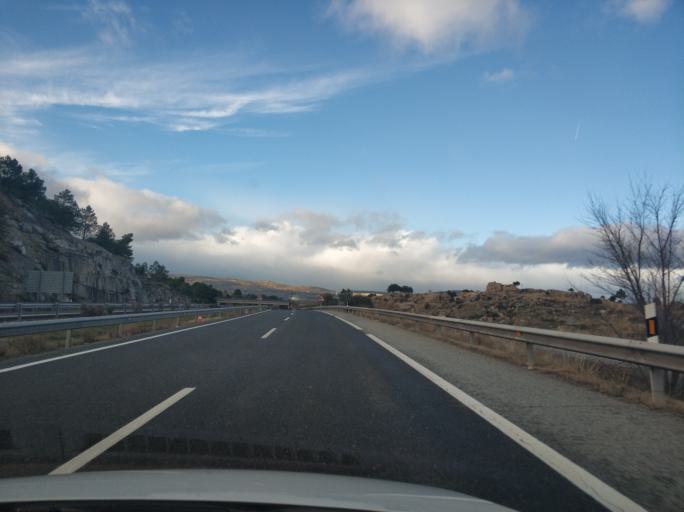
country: ES
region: Madrid
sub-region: Provincia de Madrid
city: La Cabrera
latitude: 40.8888
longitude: -3.5998
